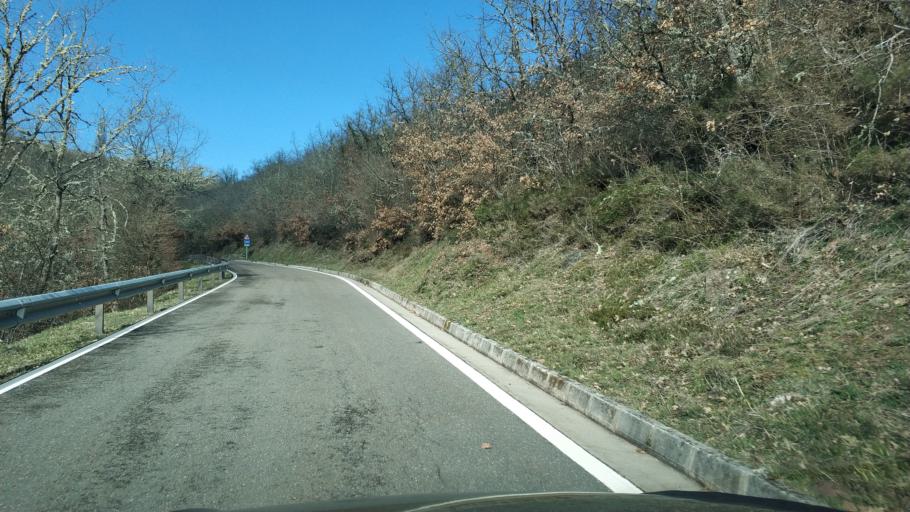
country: ES
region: Castille and Leon
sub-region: Provincia de Palencia
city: Berzosilla
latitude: 42.8990
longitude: -4.0401
